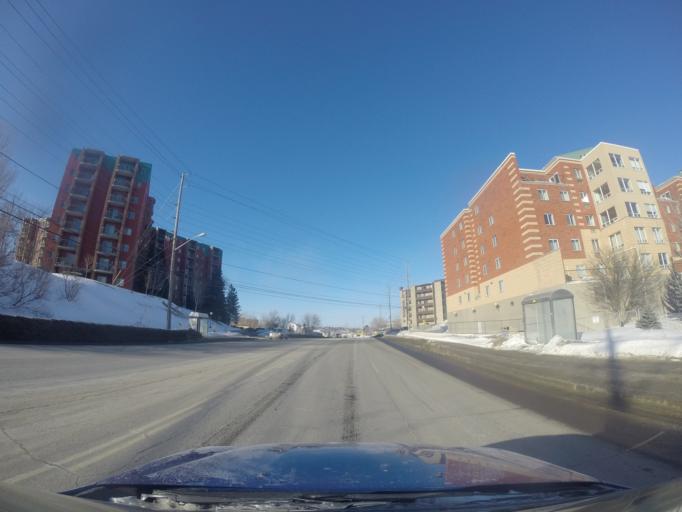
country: CA
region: Ontario
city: Greater Sudbury
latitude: 46.4590
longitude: -81.0013
